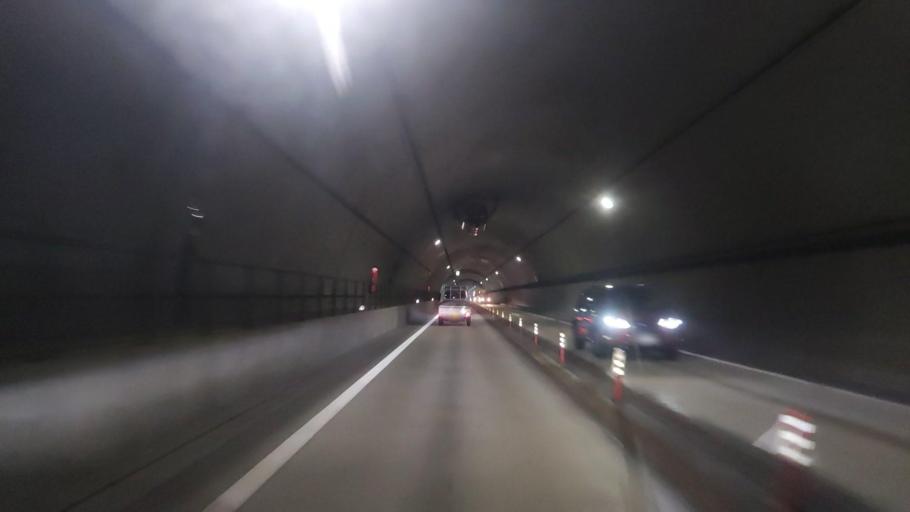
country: JP
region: Wakayama
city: Tanabe
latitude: 33.6270
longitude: 135.4163
